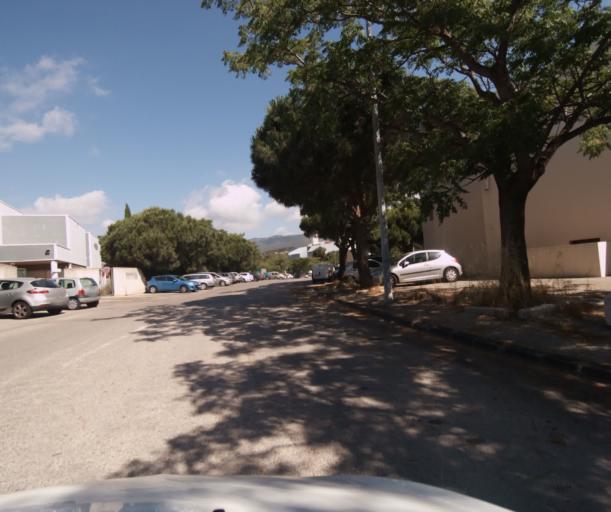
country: FR
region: Provence-Alpes-Cote d'Azur
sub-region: Departement du Var
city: La Seyne-sur-Mer
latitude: 43.1226
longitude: 5.8922
